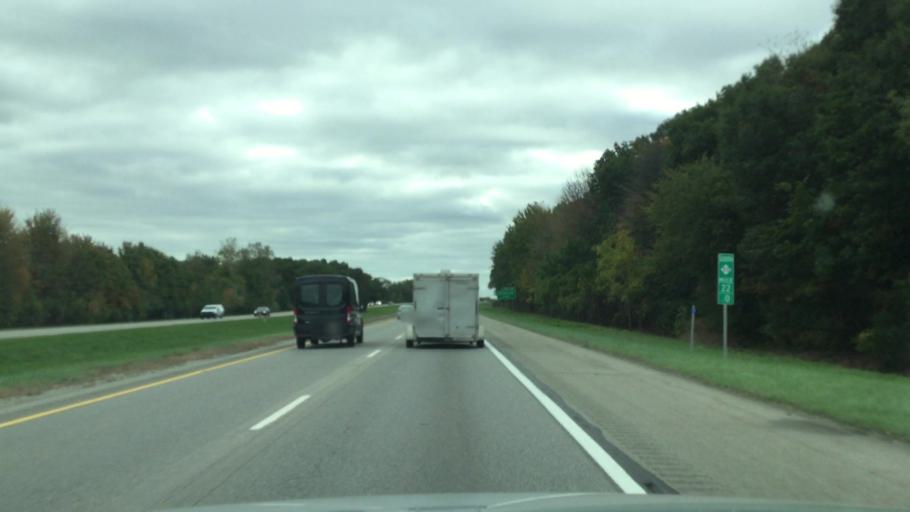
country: US
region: Michigan
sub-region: Macomb County
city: Shelby
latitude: 42.6898
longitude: -83.0197
